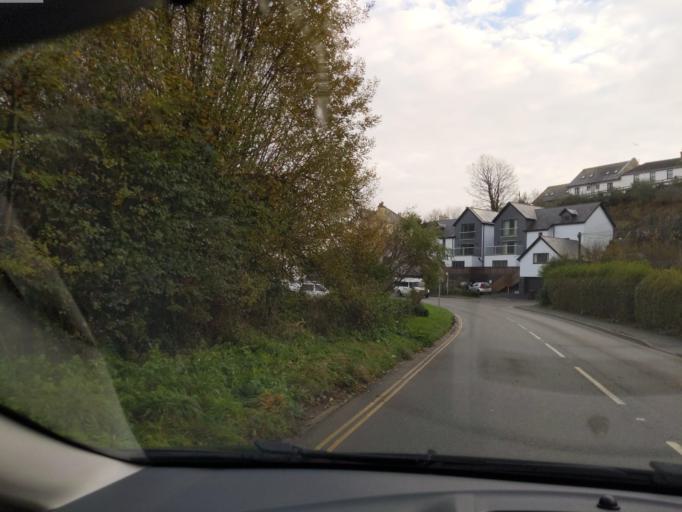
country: GB
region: England
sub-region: Cornwall
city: Looe
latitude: 50.3664
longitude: -4.3884
